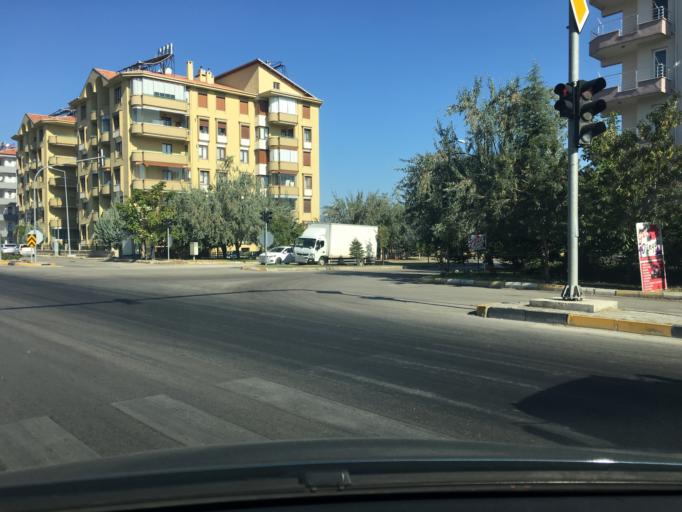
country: TR
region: Isparta
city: Isparta
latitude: 37.7883
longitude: 30.5551
